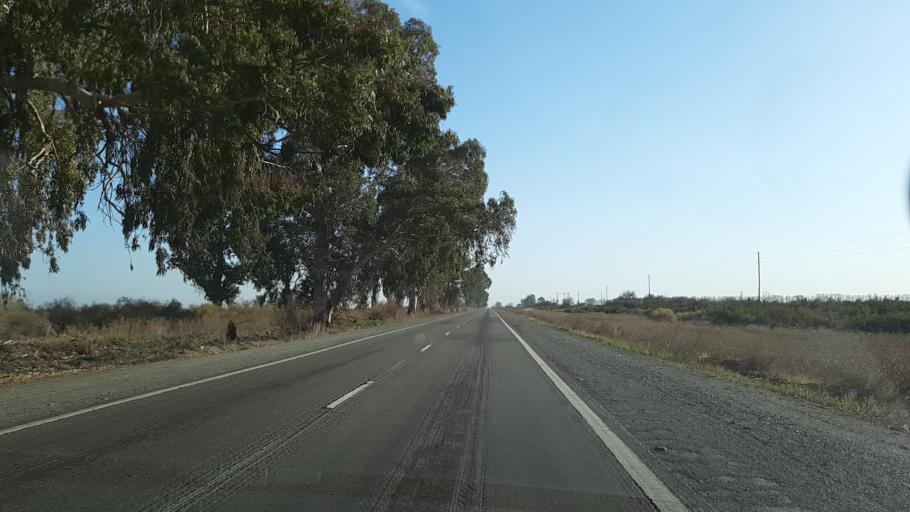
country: AR
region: Mendoza
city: General Lavalle
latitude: -32.5178
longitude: -68.6449
